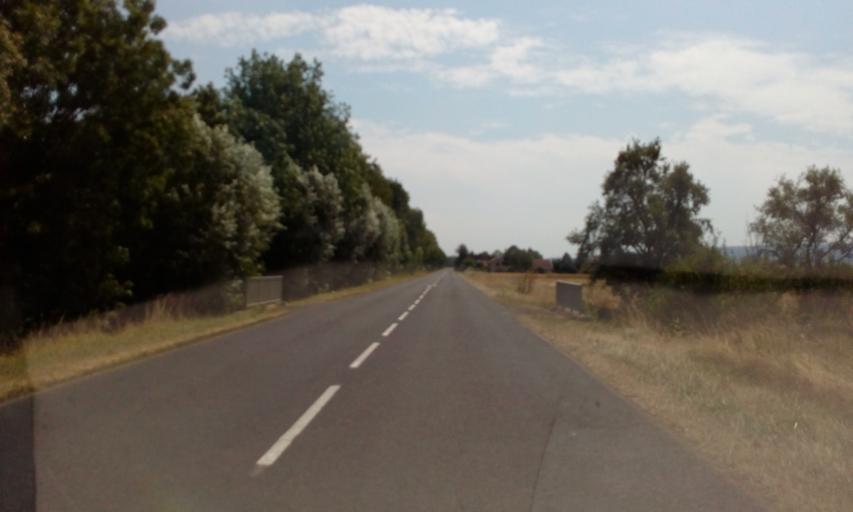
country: FR
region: Lorraine
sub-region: Departement de la Meuse
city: Vigneulles-les-Hattonchatel
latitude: 49.0812
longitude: 5.6371
